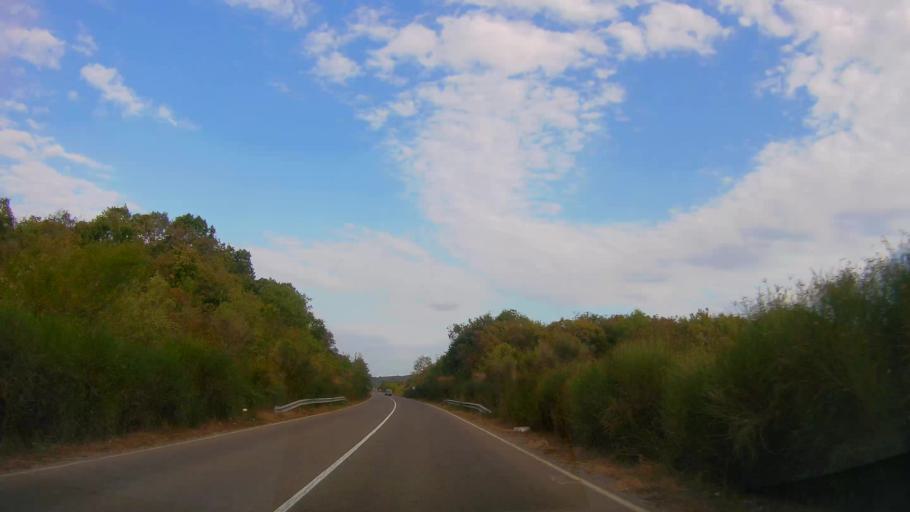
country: BG
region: Burgas
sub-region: Obshtina Sozopol
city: Sozopol
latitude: 42.3480
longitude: 27.7134
